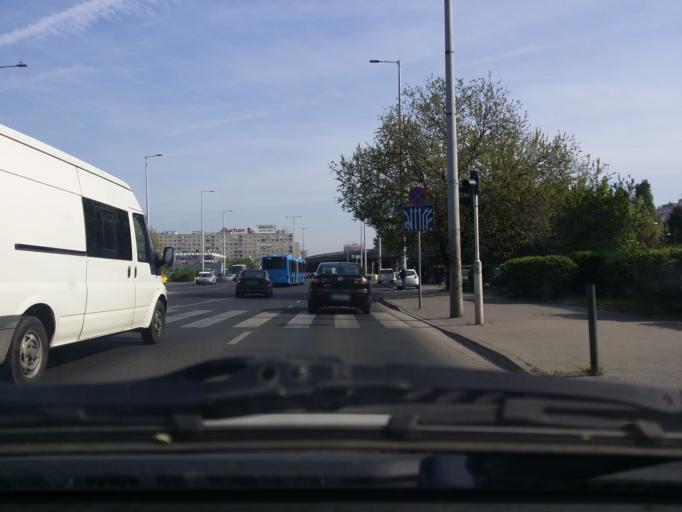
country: HU
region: Budapest
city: Budapest III. keruelet
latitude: 47.5389
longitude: 19.0407
